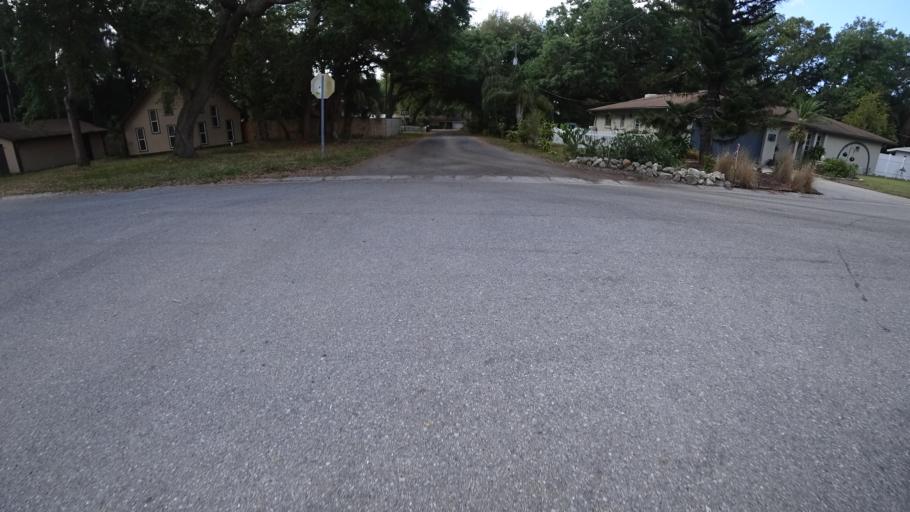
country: US
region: Florida
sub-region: Manatee County
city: Whitfield
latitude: 27.4203
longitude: -82.5687
